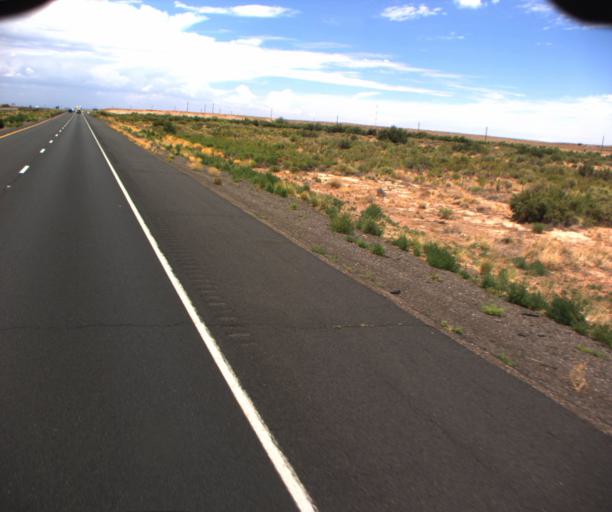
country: US
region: Arizona
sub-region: Navajo County
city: Winslow
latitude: 35.0028
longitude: -110.6059
